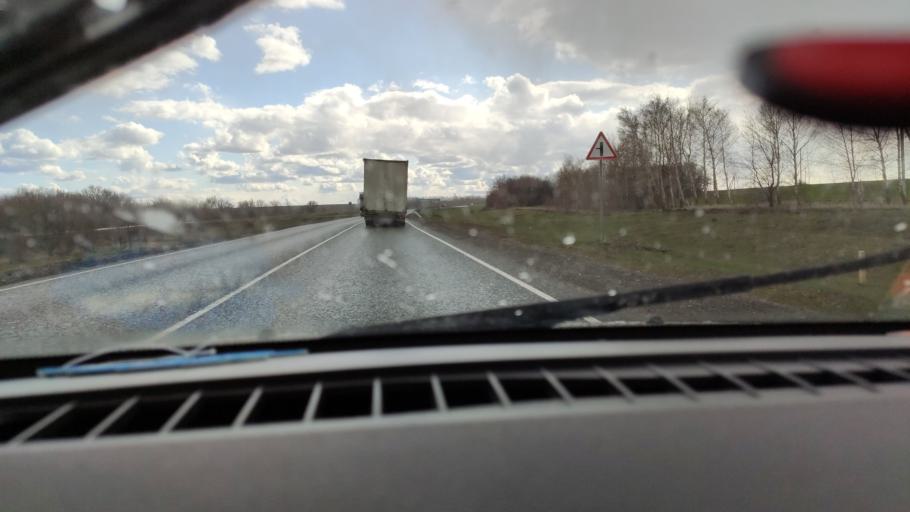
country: RU
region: Saratov
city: Balakovo
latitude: 52.1082
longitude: 47.7457
